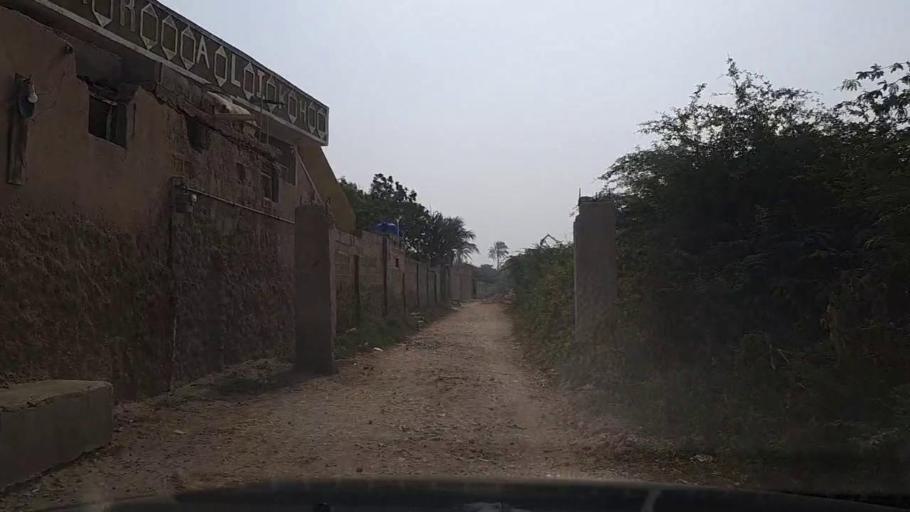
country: PK
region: Sindh
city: Thatta
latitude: 24.5542
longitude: 67.8392
